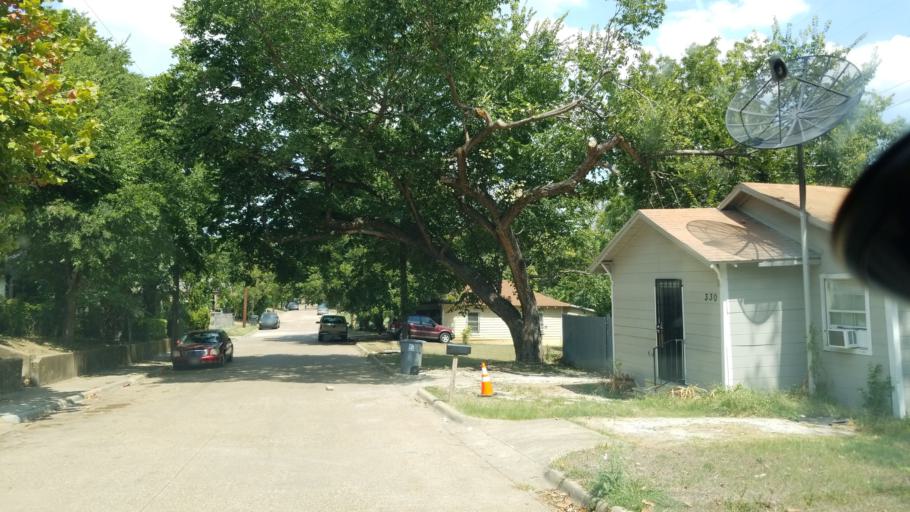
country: US
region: Texas
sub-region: Dallas County
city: Dallas
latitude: 32.7522
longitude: -96.8038
